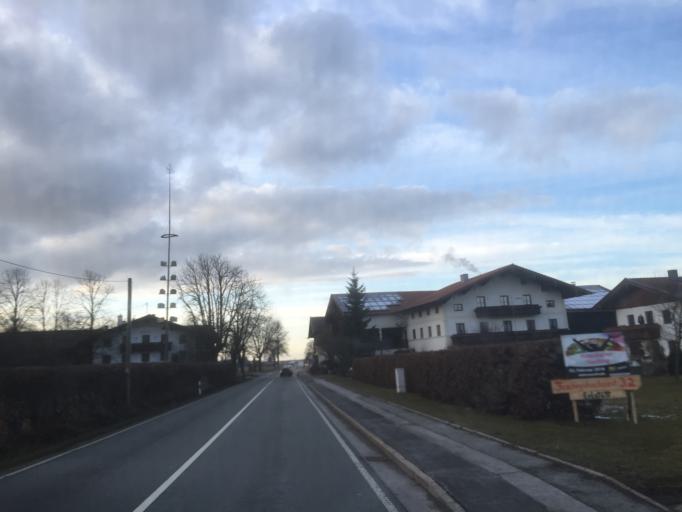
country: DE
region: Bavaria
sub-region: Upper Bavaria
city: Nussdorf
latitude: 47.8866
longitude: 12.5771
